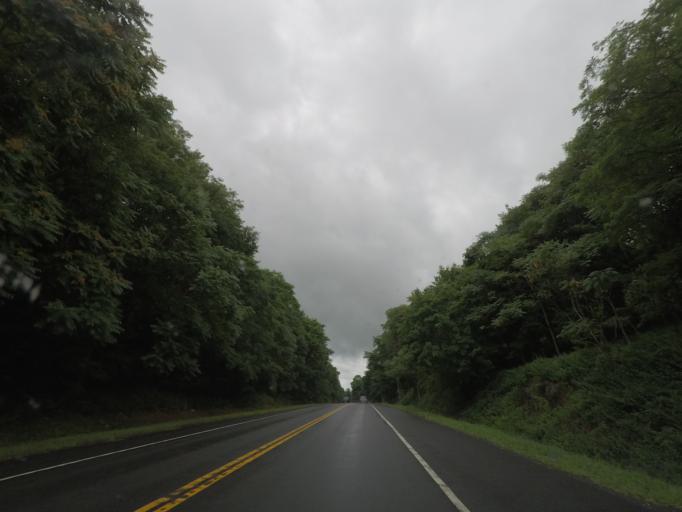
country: US
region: New York
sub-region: Rensselaer County
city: Hampton Manor
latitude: 42.6243
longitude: -73.7213
